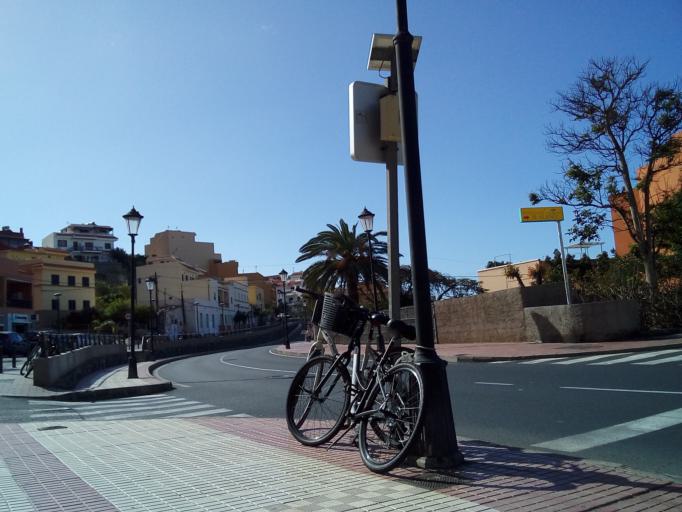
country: ES
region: Canary Islands
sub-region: Provincia de Santa Cruz de Tenerife
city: Alajero
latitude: 28.0853
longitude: -17.3344
